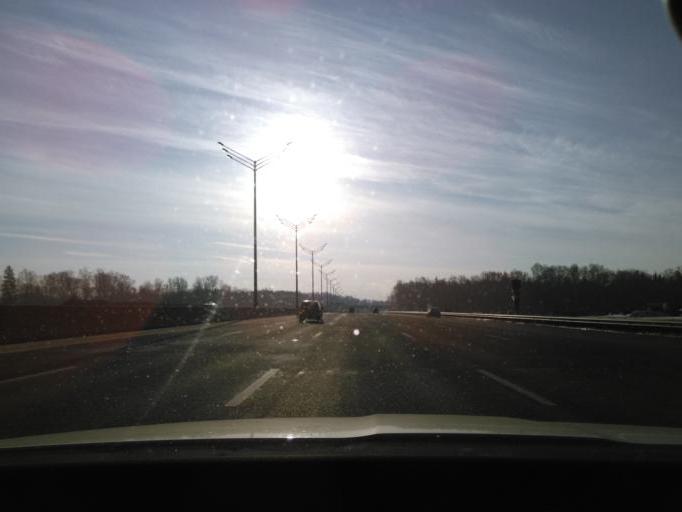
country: RU
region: Moscow
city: Khimki
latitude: 55.9484
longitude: 37.4390
